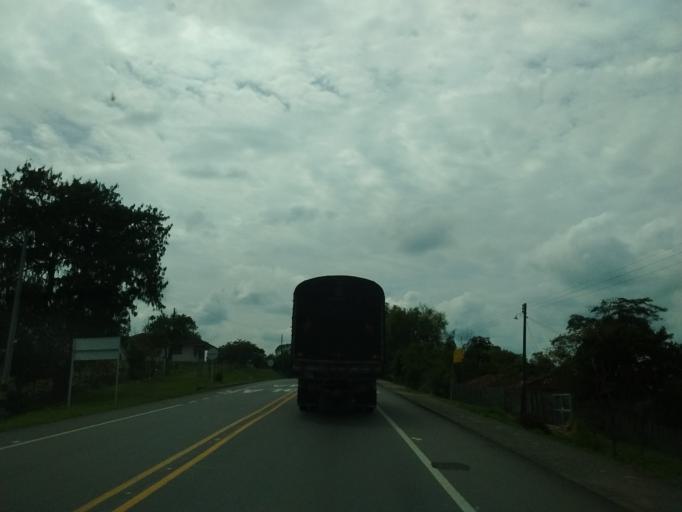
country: CO
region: Cauca
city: Morales
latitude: 2.7424
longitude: -76.5486
